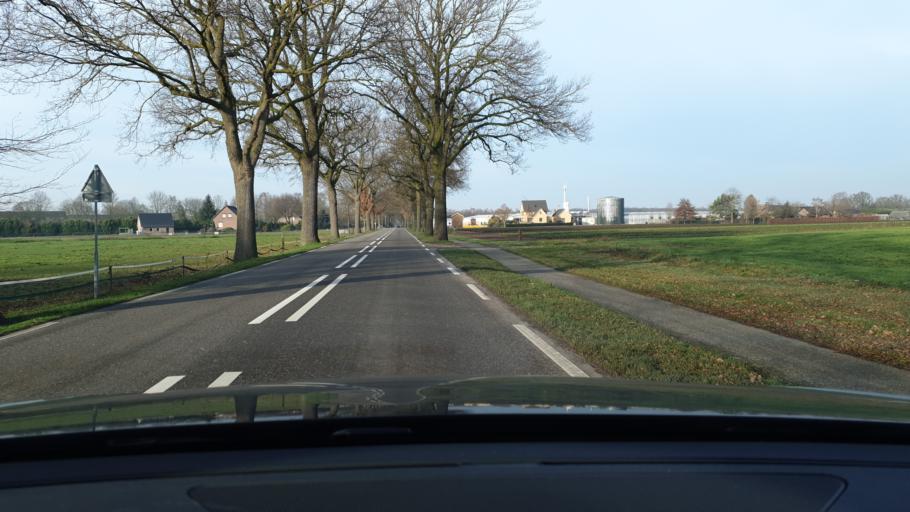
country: NL
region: Limburg
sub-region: Gemeente Peel en Maas
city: Maasbree
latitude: 51.4337
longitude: 6.0903
